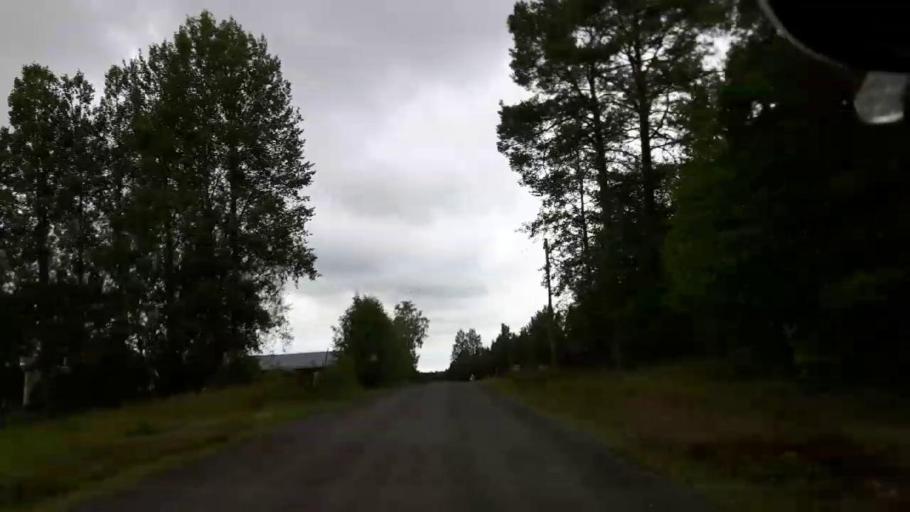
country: SE
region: Jaemtland
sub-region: OEstersunds Kommun
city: Ostersund
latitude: 63.0205
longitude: 14.5861
